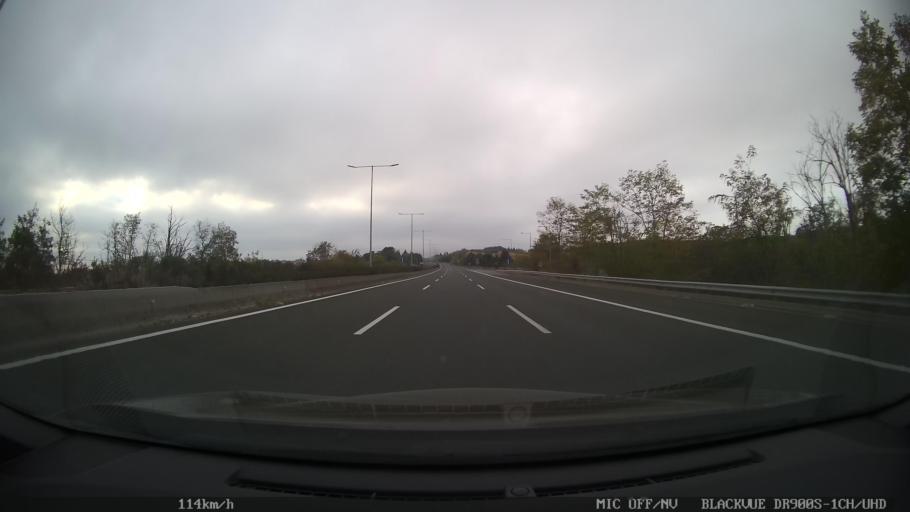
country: GR
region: Central Macedonia
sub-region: Nomos Pierias
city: Makrygialos
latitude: 40.4595
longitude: 22.5784
